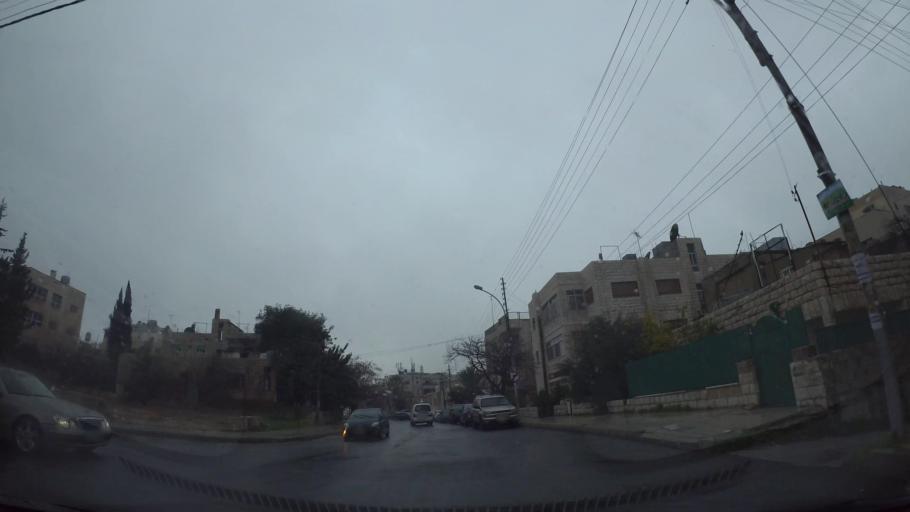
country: JO
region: Amman
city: Amman
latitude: 31.9755
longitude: 35.9148
